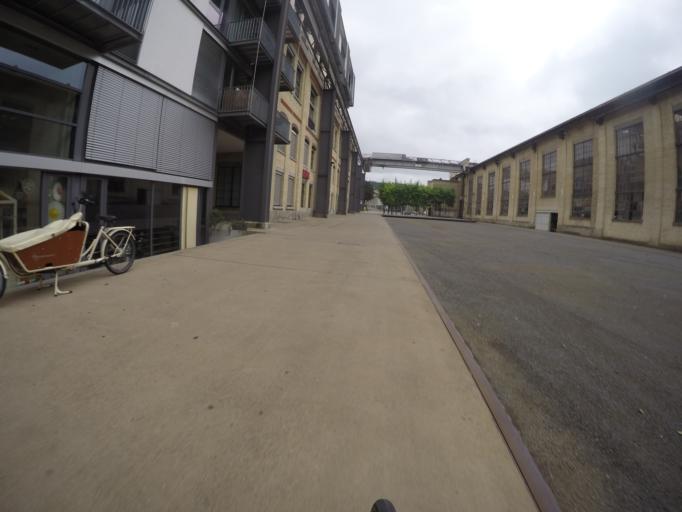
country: CH
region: Zurich
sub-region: Bezirk Winterthur
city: Stadt Winterthur (Kreis 1)
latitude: 47.4969
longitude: 8.7181
